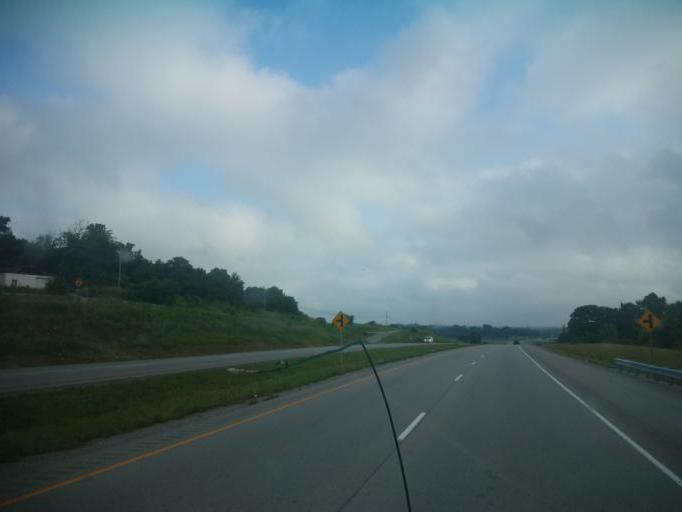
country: US
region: Kentucky
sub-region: Clinton County
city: Albany
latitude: 36.7441
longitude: -85.1358
